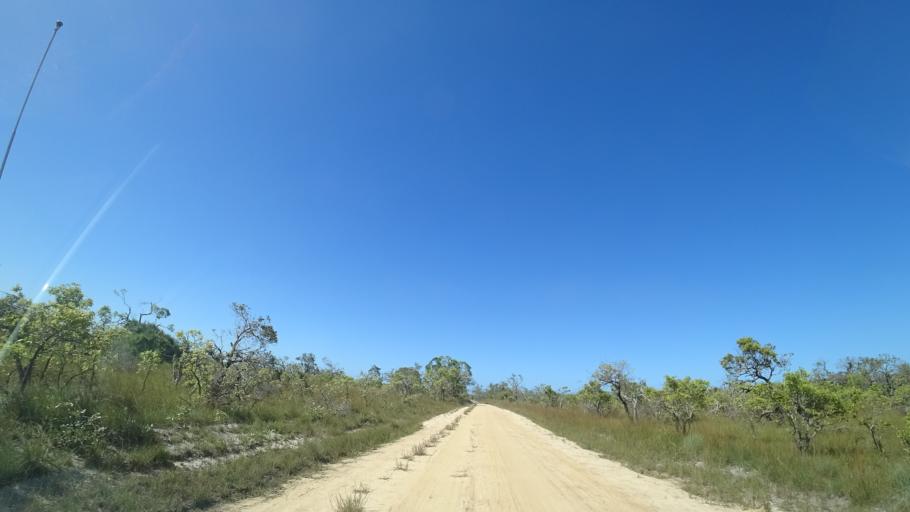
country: MZ
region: Sofala
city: Beira
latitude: -19.5726
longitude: 35.2312
